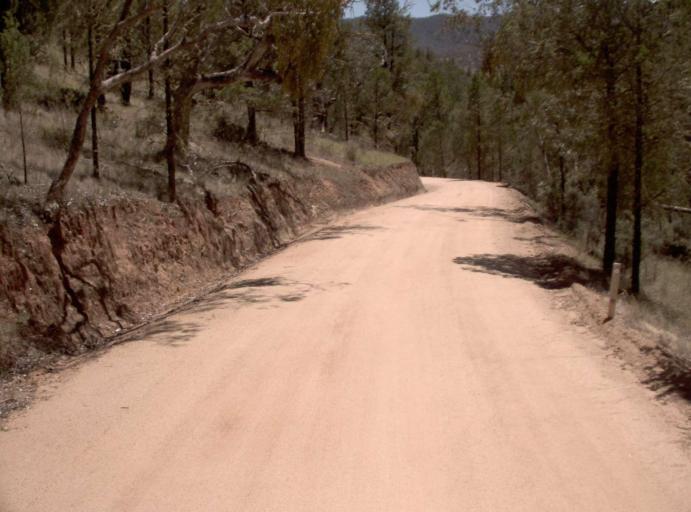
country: AU
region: New South Wales
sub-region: Snowy River
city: Jindabyne
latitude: -36.9596
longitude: 148.3236
